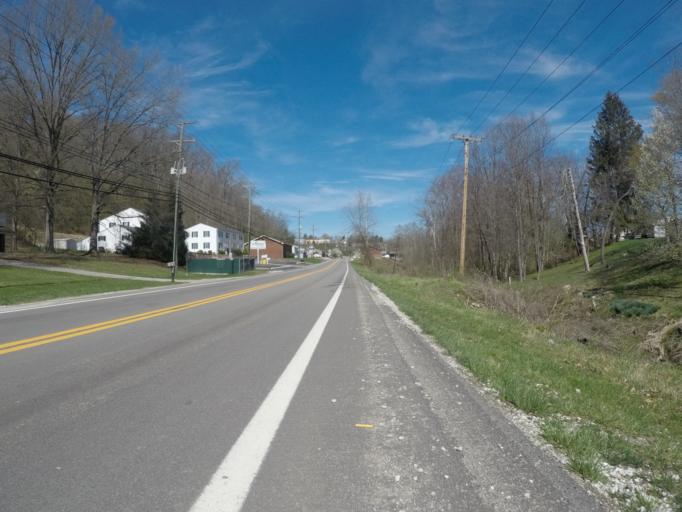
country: US
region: West Virginia
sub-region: Cabell County
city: Pea Ridge
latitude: 38.4056
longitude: -82.3199
